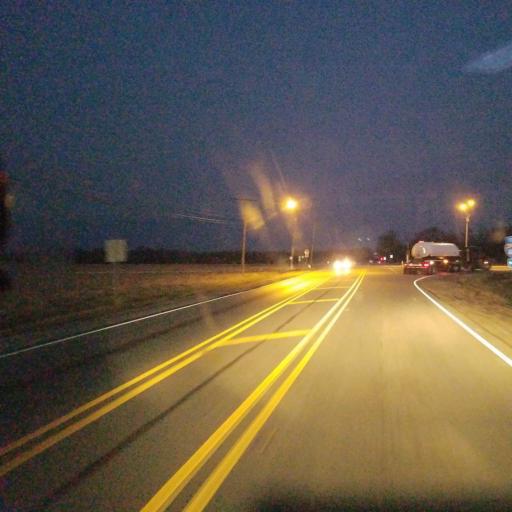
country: US
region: Illinois
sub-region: Peoria County
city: Bellevue
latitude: 40.6933
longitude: -89.6940
